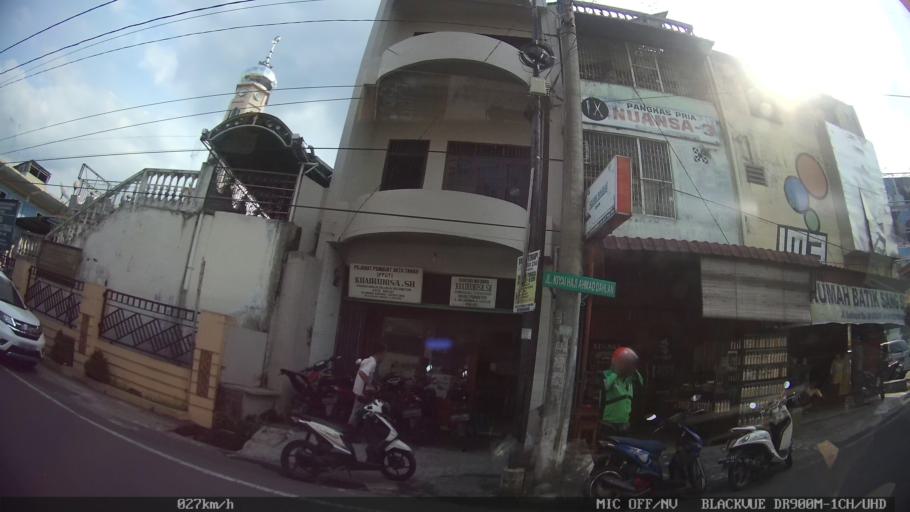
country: ID
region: North Sumatra
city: Binjai
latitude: 3.6045
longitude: 98.4857
